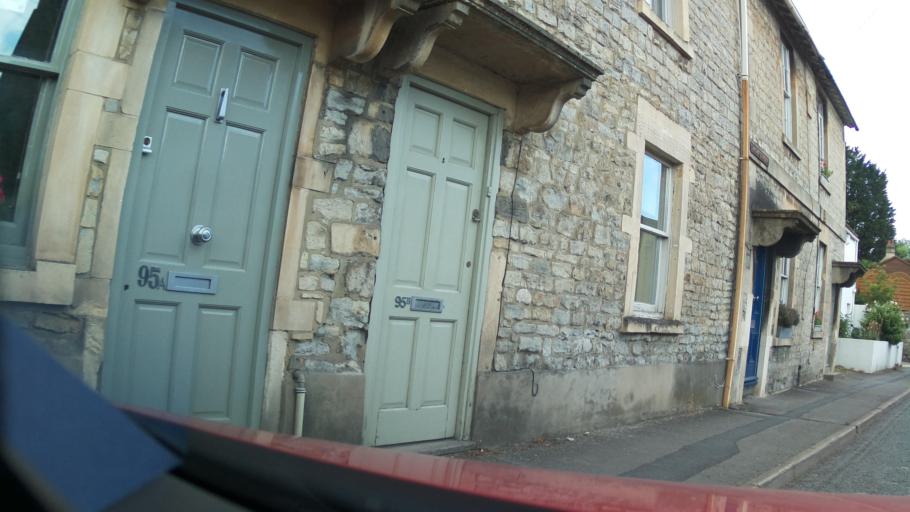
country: GB
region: England
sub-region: Bath and North East Somerset
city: Bath
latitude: 51.3981
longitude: -2.3954
